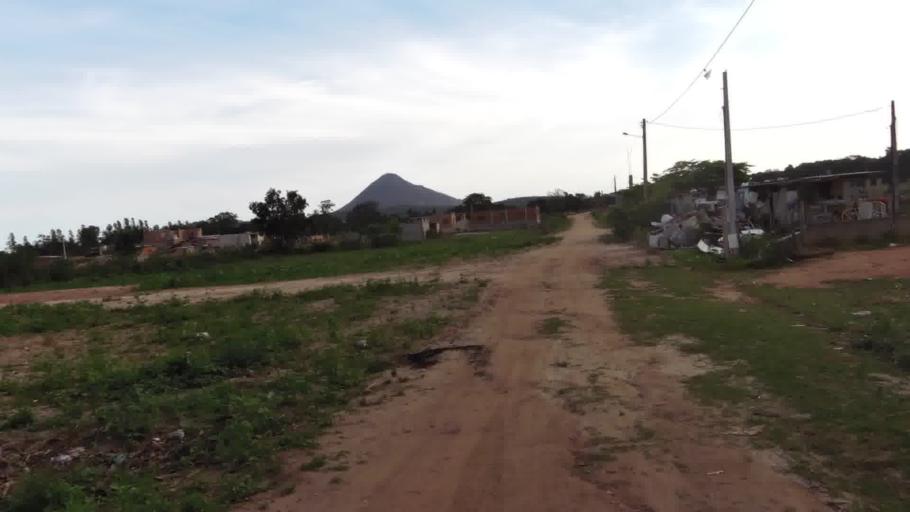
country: BR
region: Espirito Santo
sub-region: Piuma
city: Piuma
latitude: -20.8417
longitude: -40.7508
